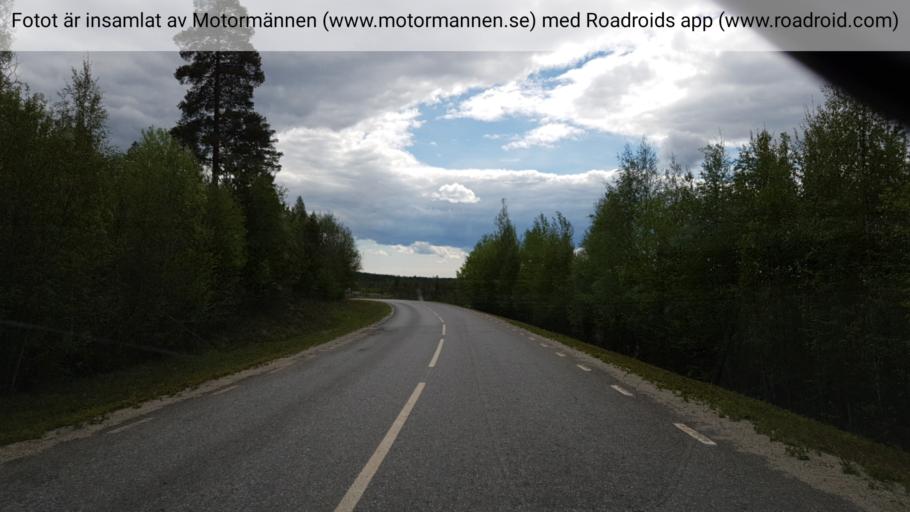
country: SE
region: Vaesterbotten
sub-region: Vindelns Kommun
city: Vindeln
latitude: 64.3452
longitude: 19.6234
